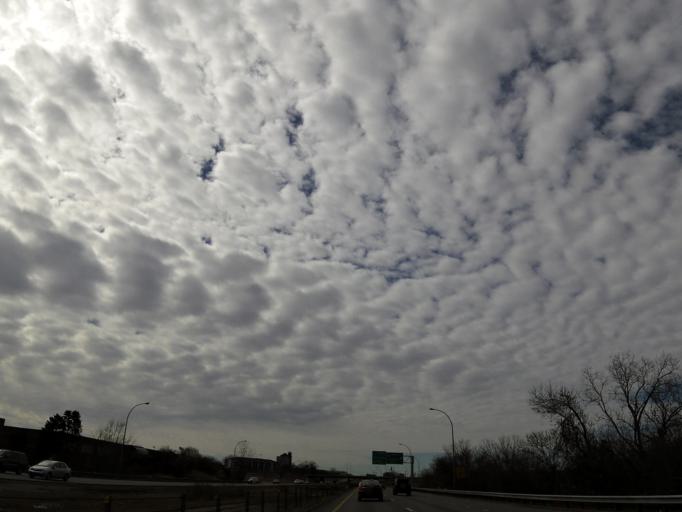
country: US
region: Minnesota
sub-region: Ramsey County
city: Roseville
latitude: 45.0104
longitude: -93.1605
